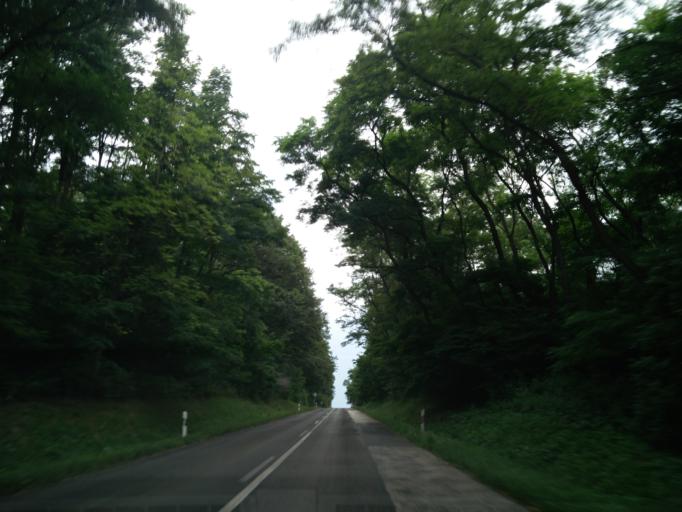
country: HU
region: Vas
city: Vasvar
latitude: 47.0251
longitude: 16.8177
